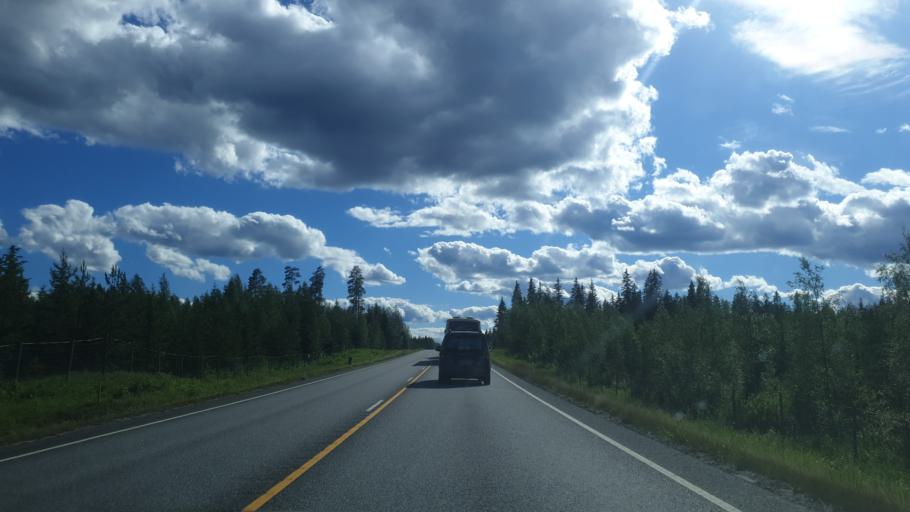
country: FI
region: Southern Savonia
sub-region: Pieksaemaeki
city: Juva
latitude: 61.8354
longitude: 27.6534
